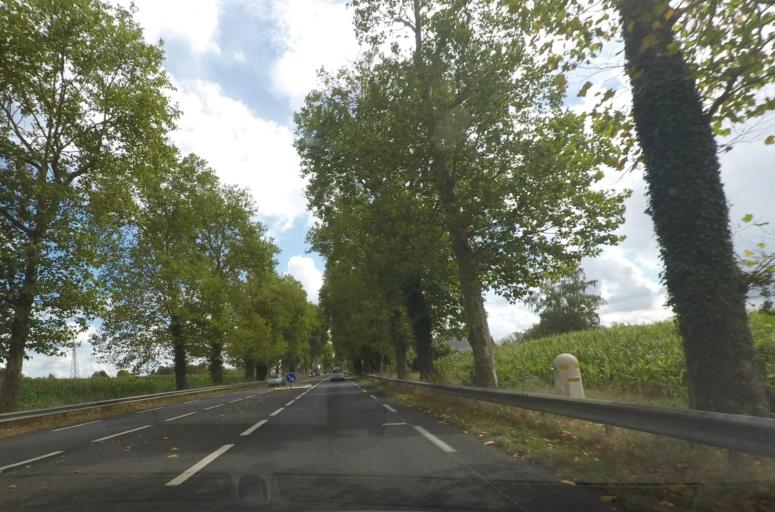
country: FR
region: Pays de la Loire
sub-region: Departement de la Sarthe
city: La Fleche
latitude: 47.6944
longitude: -0.1126
